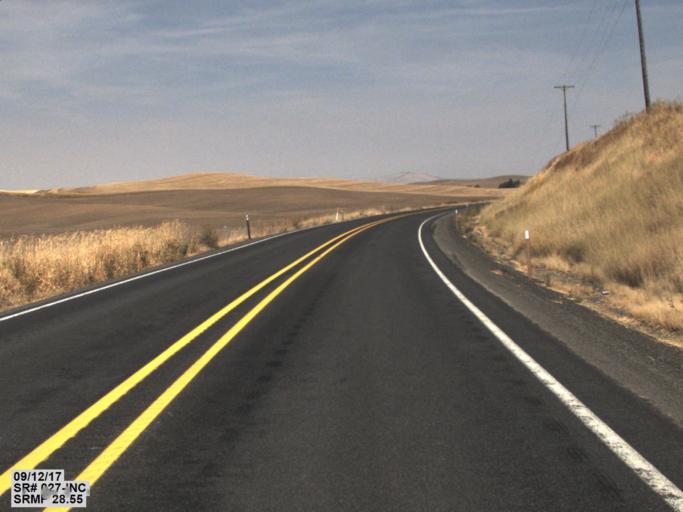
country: US
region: Washington
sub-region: Whitman County
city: Colfax
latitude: 47.0596
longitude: -117.1533
